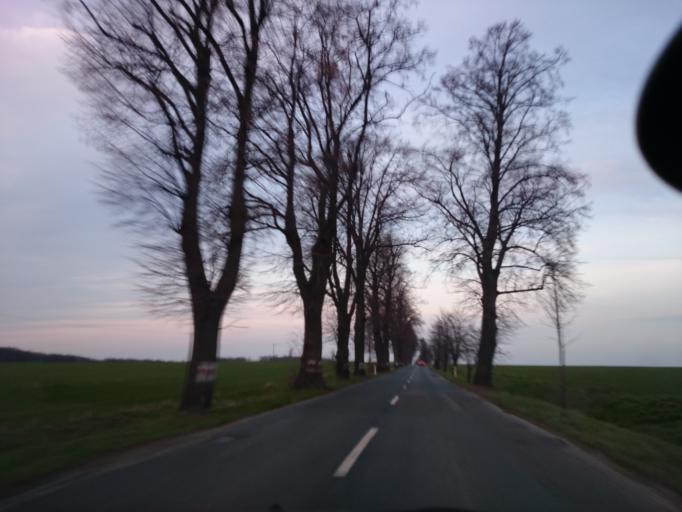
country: PL
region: Opole Voivodeship
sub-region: Powiat prudnicki
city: Lubrza
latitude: 50.3532
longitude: 17.6370
